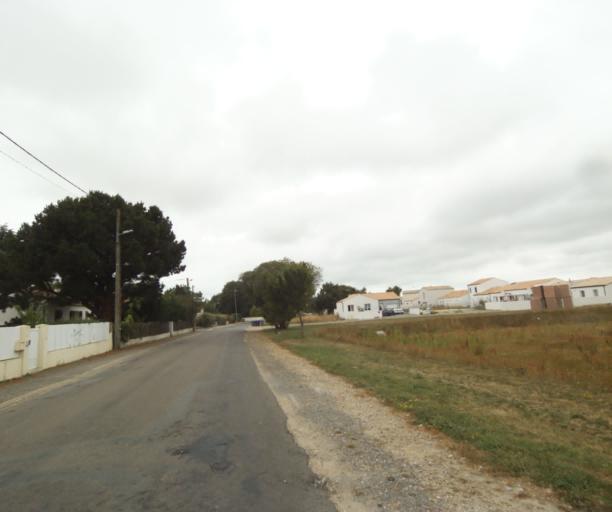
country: FR
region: Pays de la Loire
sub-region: Departement de la Vendee
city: Chateau-d'Olonne
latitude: 46.5067
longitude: -1.7444
